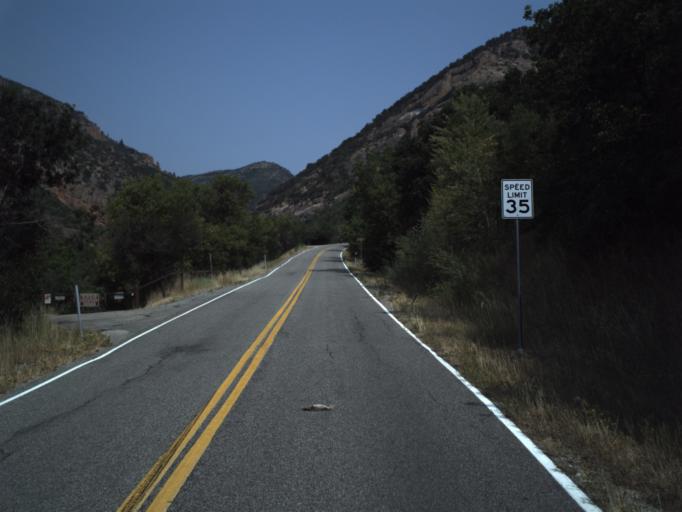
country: US
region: Utah
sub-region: Summit County
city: Summit Park
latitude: 40.8089
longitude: -111.6780
